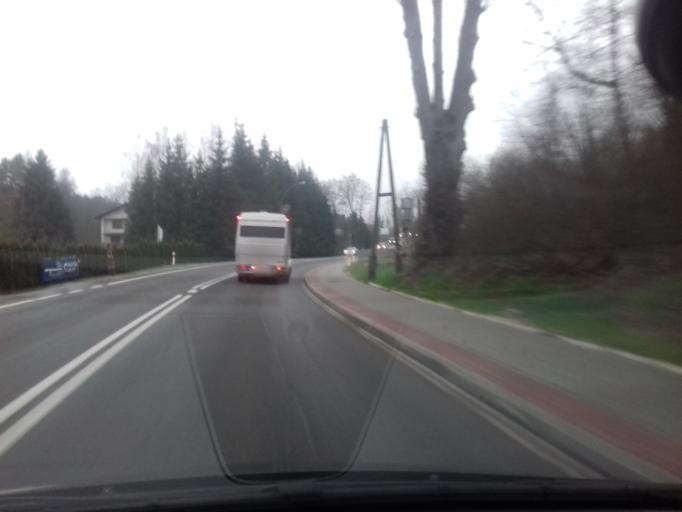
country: PL
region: Lesser Poland Voivodeship
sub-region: Powiat limanowski
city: Limanowa
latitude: 49.7203
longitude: 20.3982
